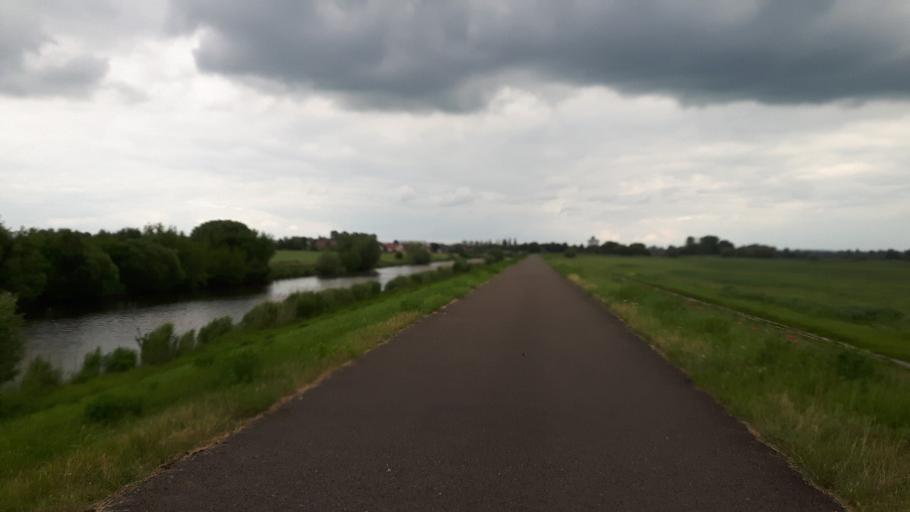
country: DE
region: Brandenburg
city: Schwedt (Oder)
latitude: 53.0404
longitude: 14.2647
